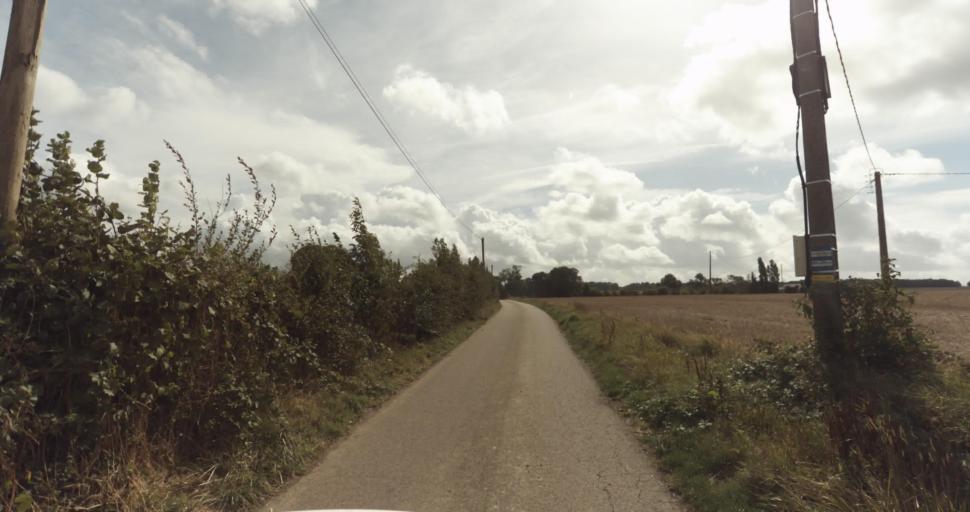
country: FR
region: Lower Normandy
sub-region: Departement de l'Orne
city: Gace
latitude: 48.8208
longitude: 0.3974
